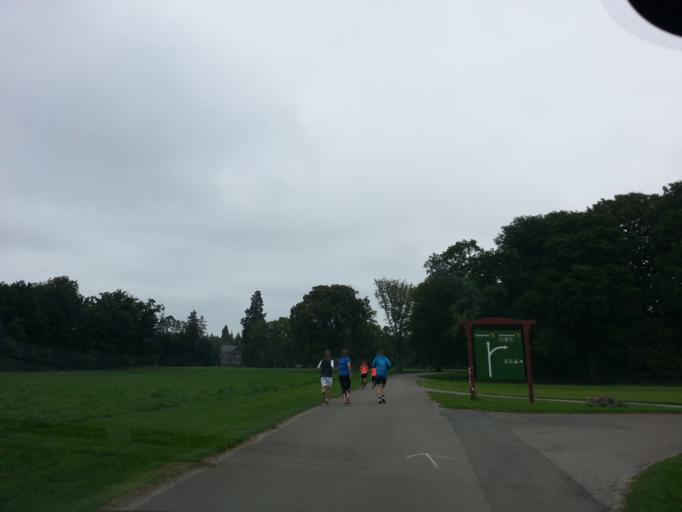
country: DK
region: Zealand
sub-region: Lolland Kommune
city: Maribo
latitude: 54.8207
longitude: 11.5020
